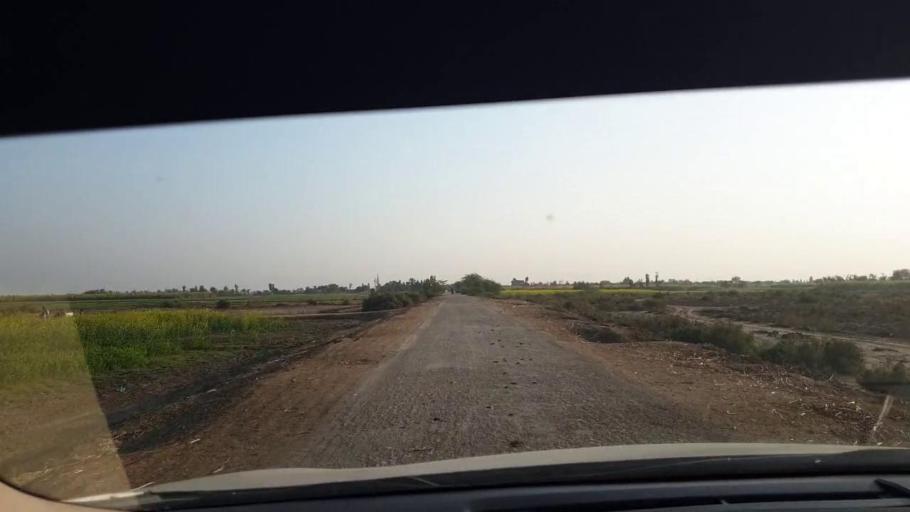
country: PK
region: Sindh
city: Berani
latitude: 25.8441
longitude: 68.8167
